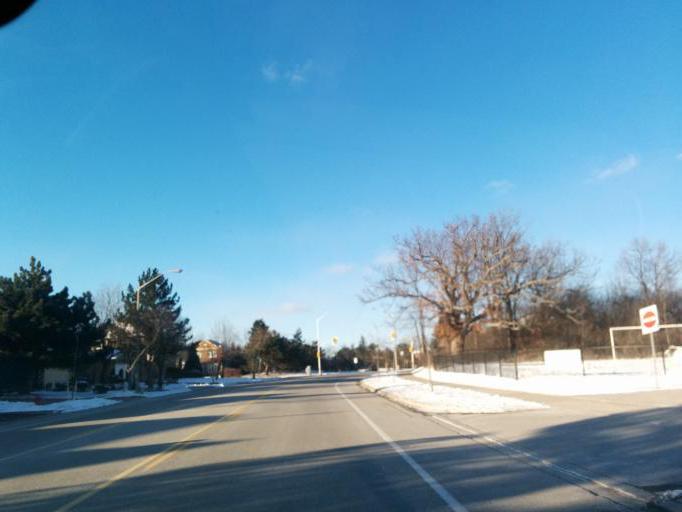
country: CA
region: Ontario
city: Oakville
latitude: 43.5018
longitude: -79.6616
